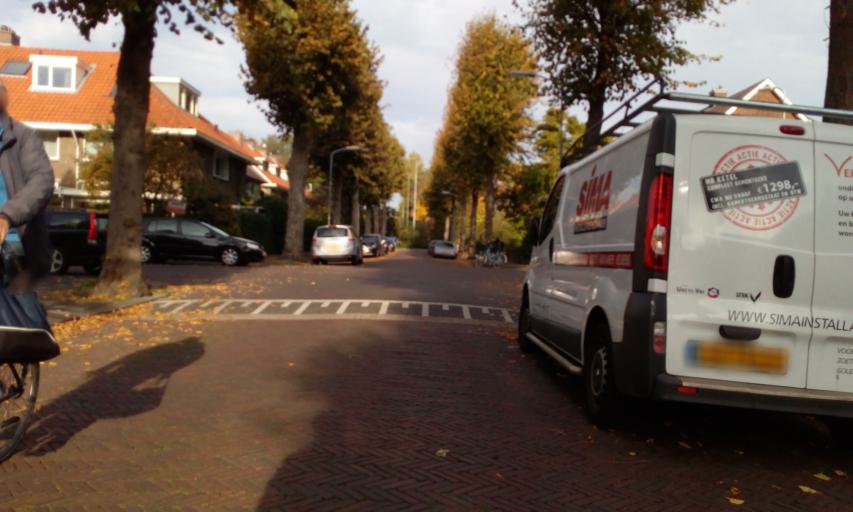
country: NL
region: South Holland
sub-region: Gemeente Leidschendam-Voorburg
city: Voorburg
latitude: 52.0834
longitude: 4.3863
